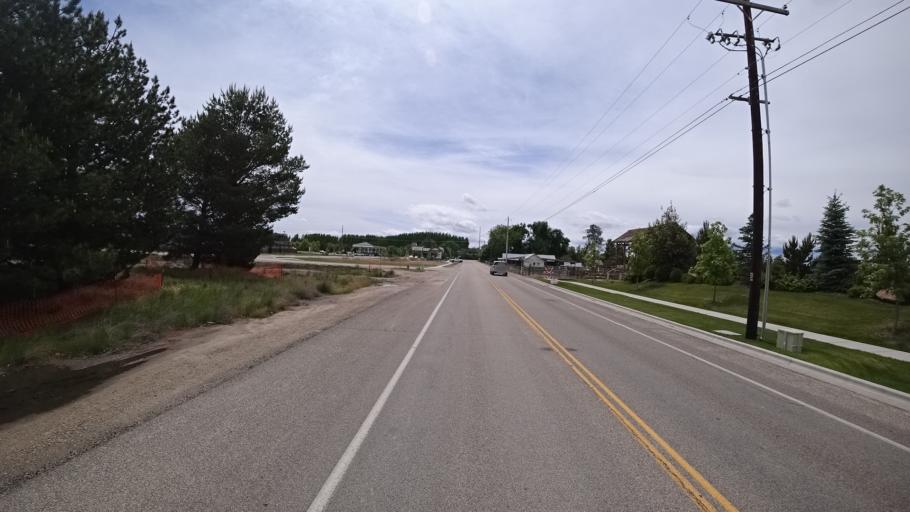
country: US
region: Idaho
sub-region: Ada County
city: Eagle
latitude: 43.6979
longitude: -116.4036
